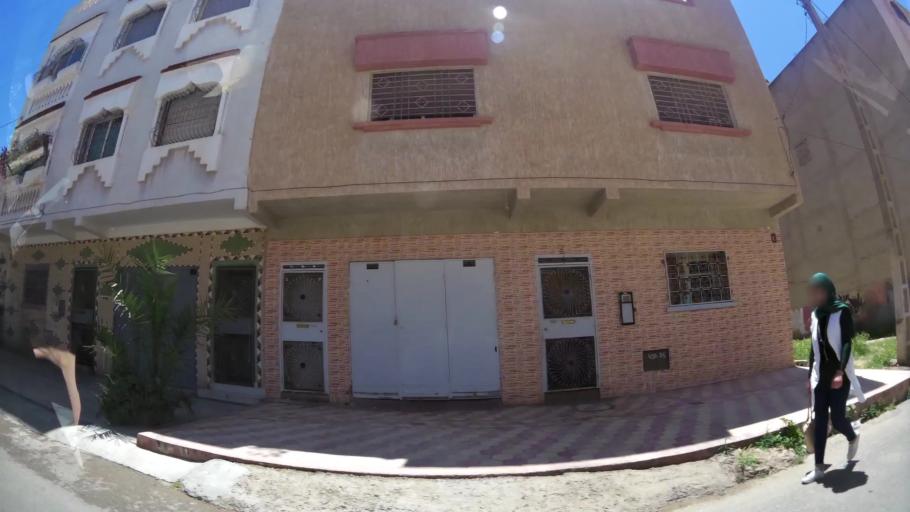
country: MA
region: Oriental
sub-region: Oujda-Angad
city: Oujda
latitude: 34.6768
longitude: -1.8803
